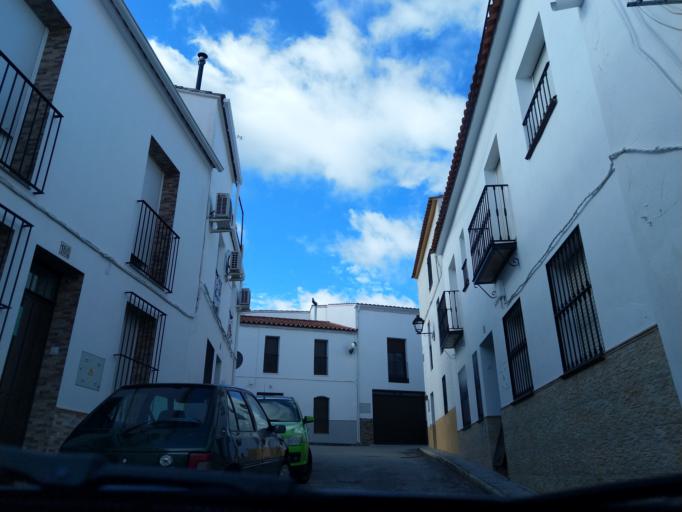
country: ES
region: Extremadura
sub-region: Provincia de Badajoz
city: Reina
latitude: 38.1516
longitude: -5.8984
